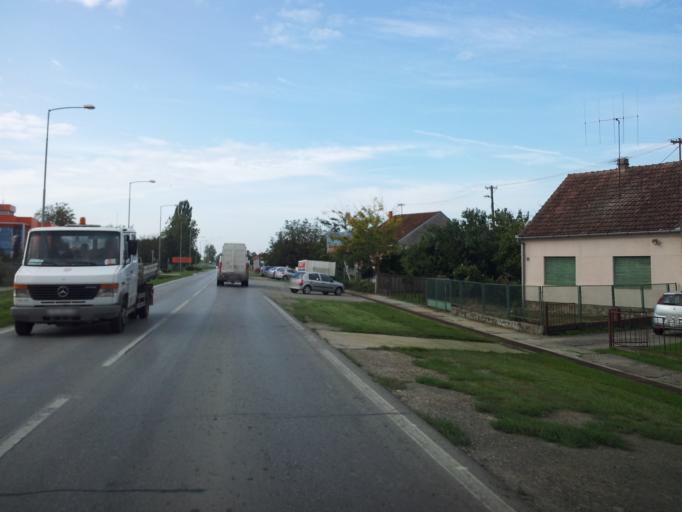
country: HR
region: Osjecko-Baranjska
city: Brijest
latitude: 45.5404
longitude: 18.6738
